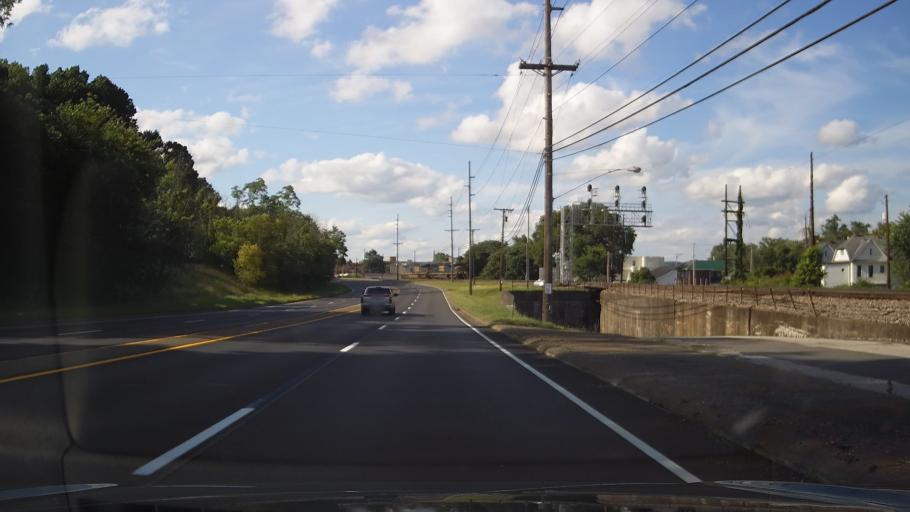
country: US
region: Kentucky
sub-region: Boyd County
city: Catlettsburg
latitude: 38.4119
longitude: -82.5992
